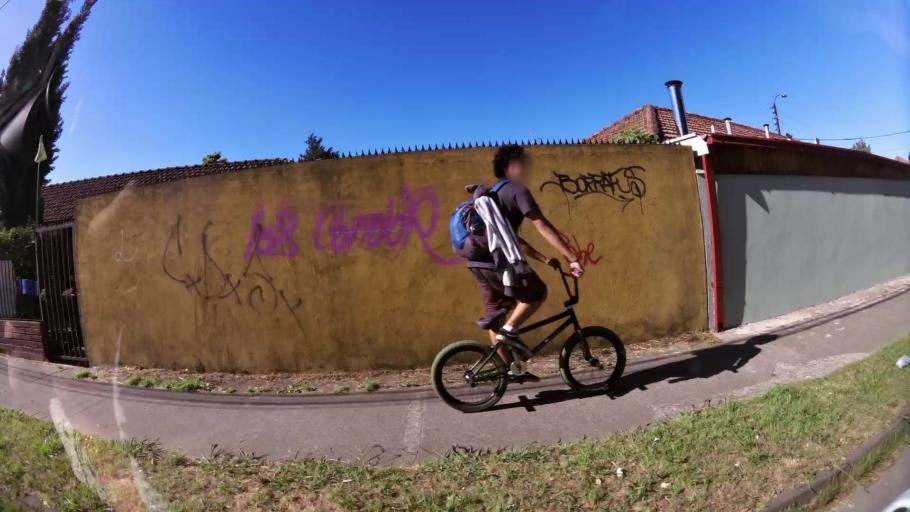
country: CL
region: Biobio
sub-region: Provincia de Concepcion
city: Concepcion
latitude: -36.8433
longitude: -73.1104
